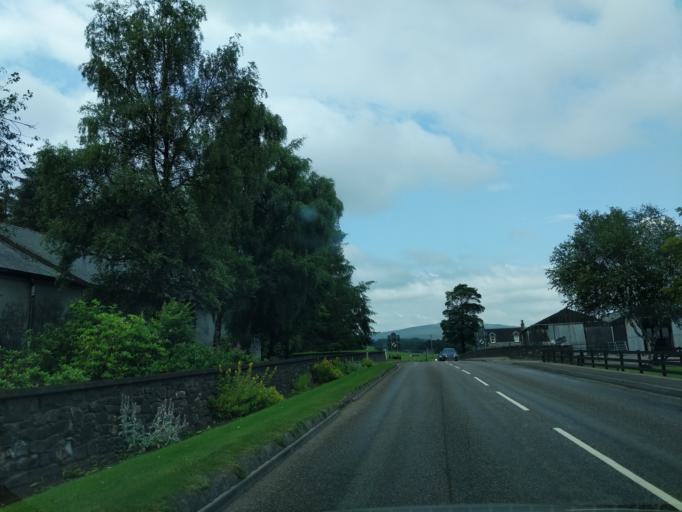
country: GB
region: Scotland
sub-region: Moray
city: Dufftown
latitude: 57.4552
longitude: -3.1309
